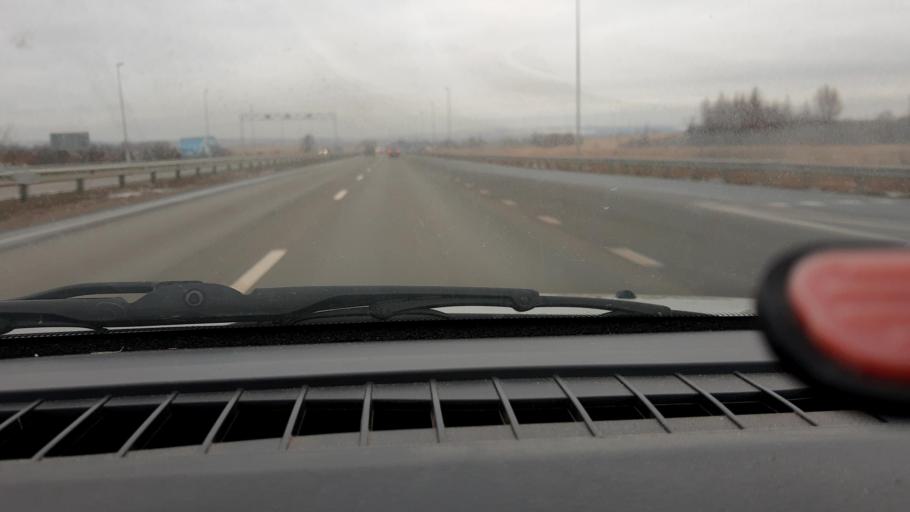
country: RU
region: Nizjnij Novgorod
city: Burevestnik
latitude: 56.1203
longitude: 43.9160
